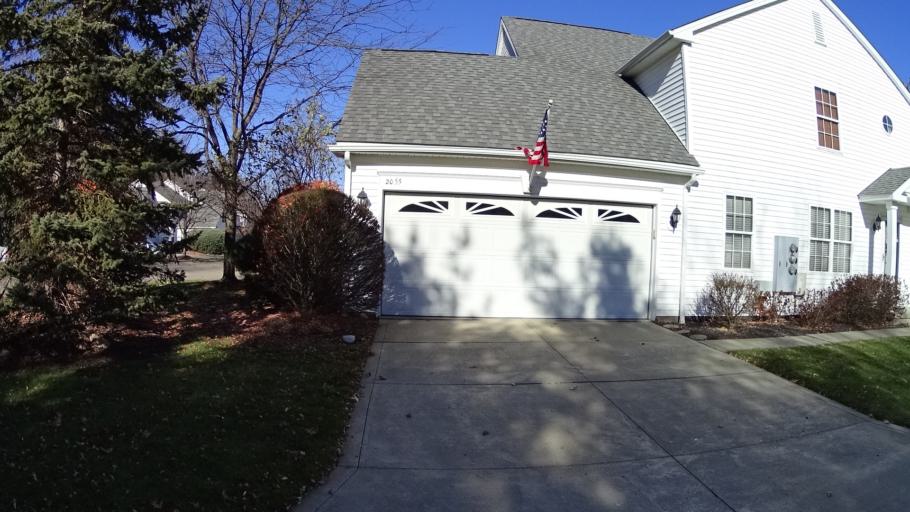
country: US
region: Ohio
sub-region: Lorain County
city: Avon Center
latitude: 41.4624
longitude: -82.0289
